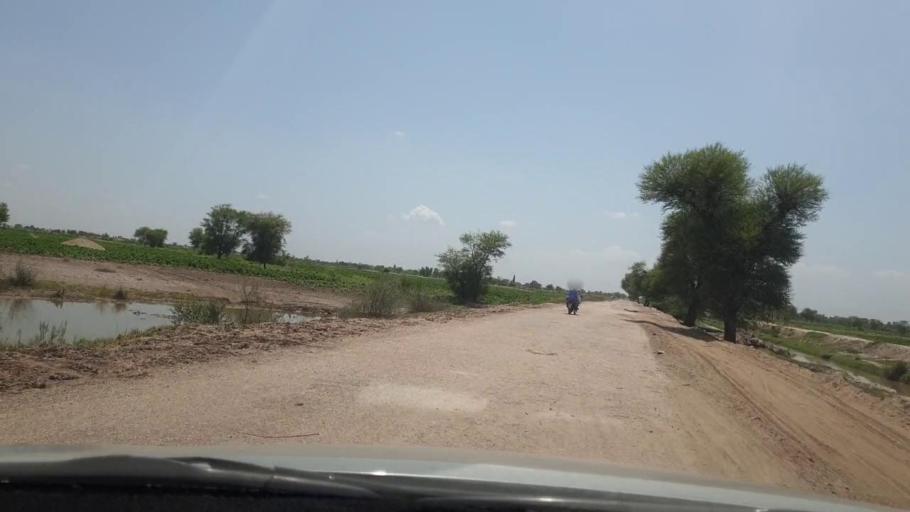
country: PK
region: Sindh
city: Pano Aqil
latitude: 27.7275
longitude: 69.1816
